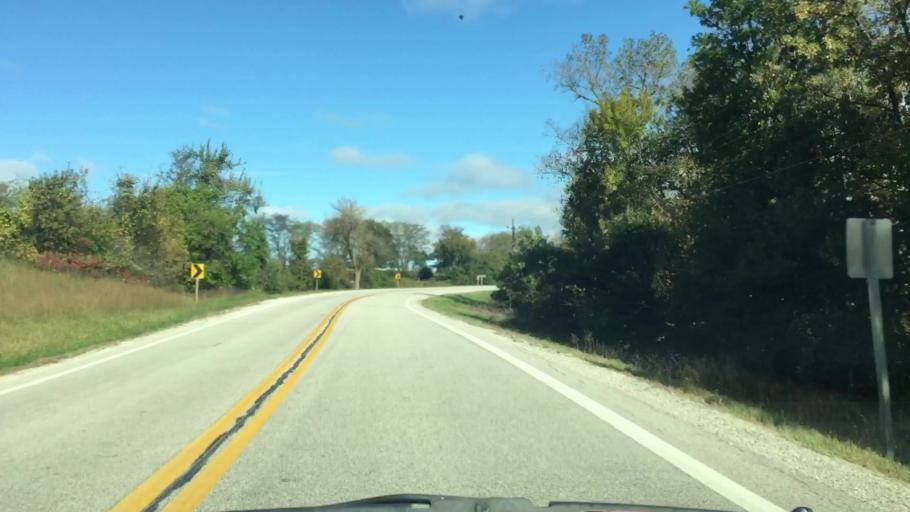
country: US
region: Iowa
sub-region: Decatur County
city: Leon
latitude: 40.7249
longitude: -93.7612
